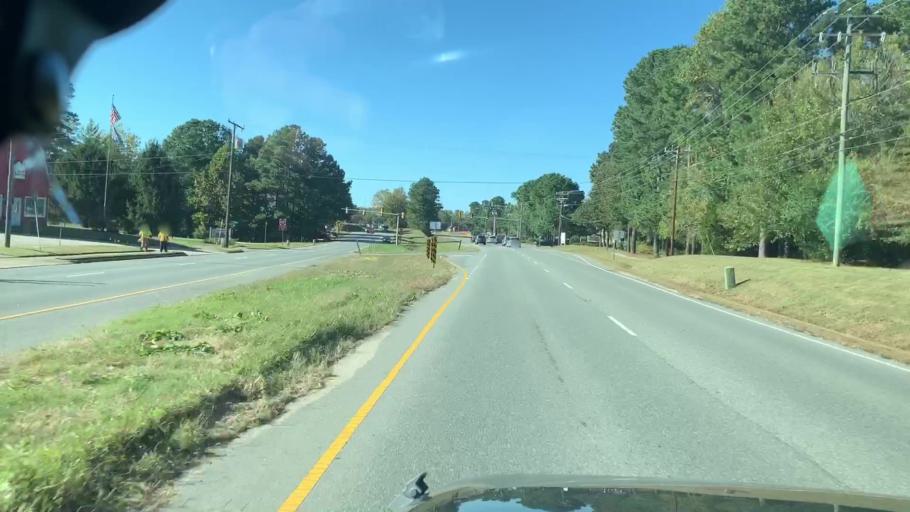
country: US
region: Virginia
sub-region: James City County
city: Williamsburg
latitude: 37.3698
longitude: -76.7724
